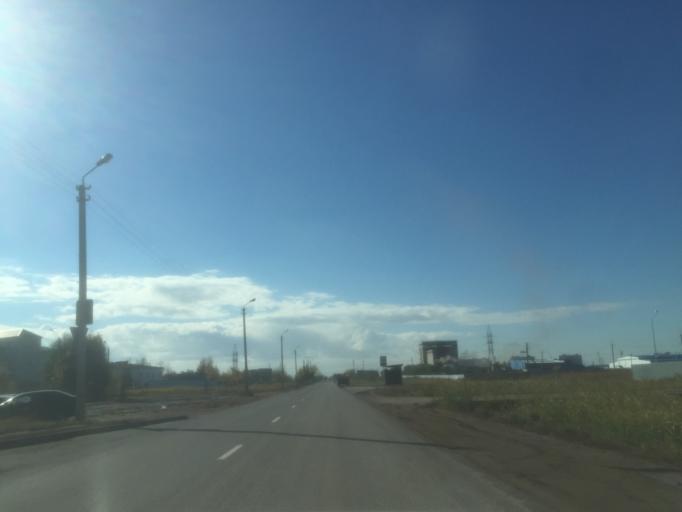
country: KZ
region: Astana Qalasy
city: Astana
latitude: 51.2051
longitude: 71.3514
